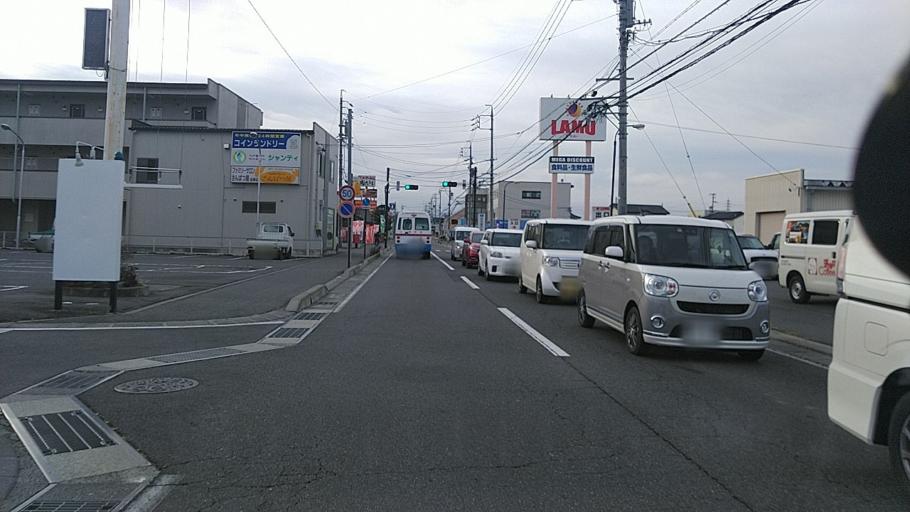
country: JP
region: Nagano
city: Matsumoto
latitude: 36.2105
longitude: 137.9795
